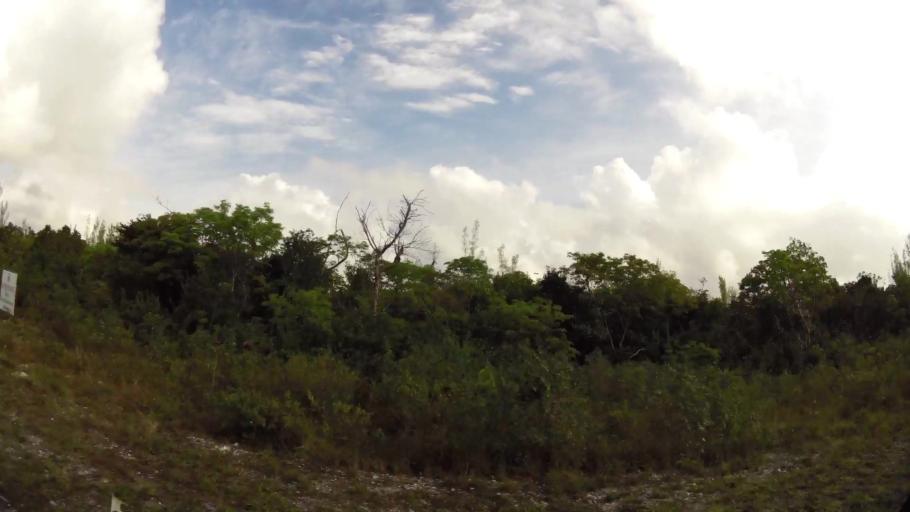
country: BS
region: Freeport
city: Lucaya
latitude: 26.5511
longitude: -78.5532
